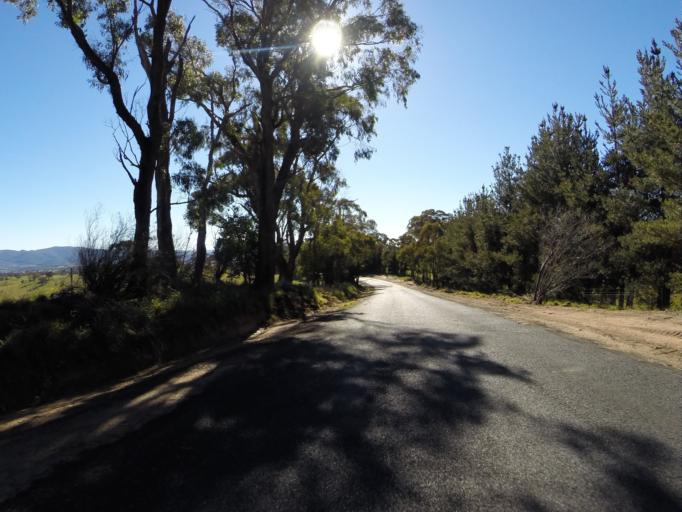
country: AU
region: New South Wales
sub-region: Oberon
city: Oberon
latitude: -33.5963
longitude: 149.8481
